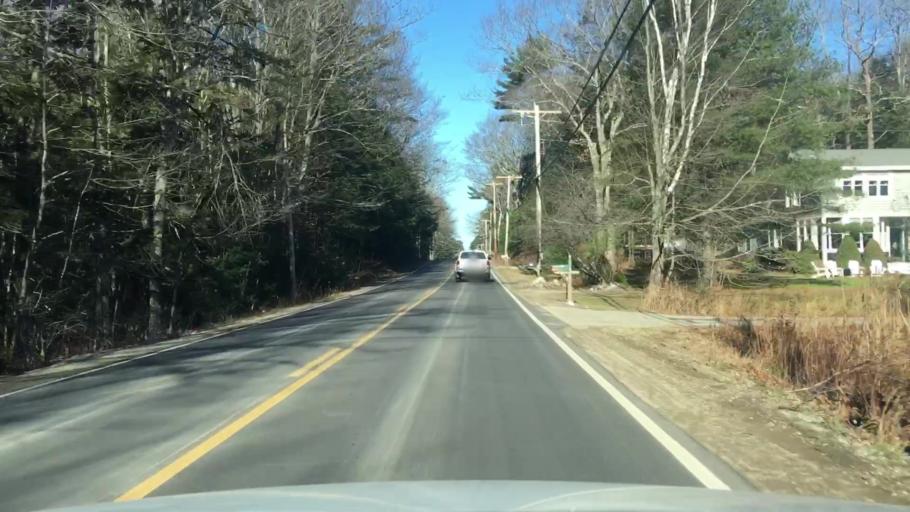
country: US
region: Maine
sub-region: York County
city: Arundel
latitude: 43.3964
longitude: -70.4845
